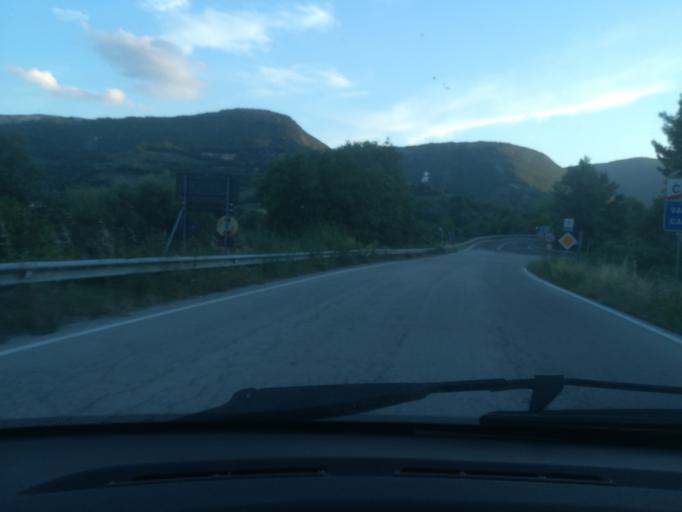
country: IT
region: The Marches
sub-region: Provincia di Macerata
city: Caldarola
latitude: 43.1462
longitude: 13.1997
